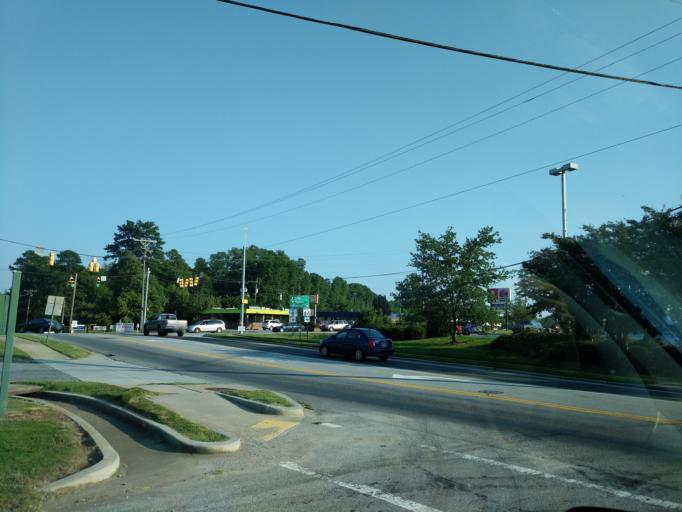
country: US
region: South Carolina
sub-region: Anderson County
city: Williamston
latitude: 34.6440
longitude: -82.4664
